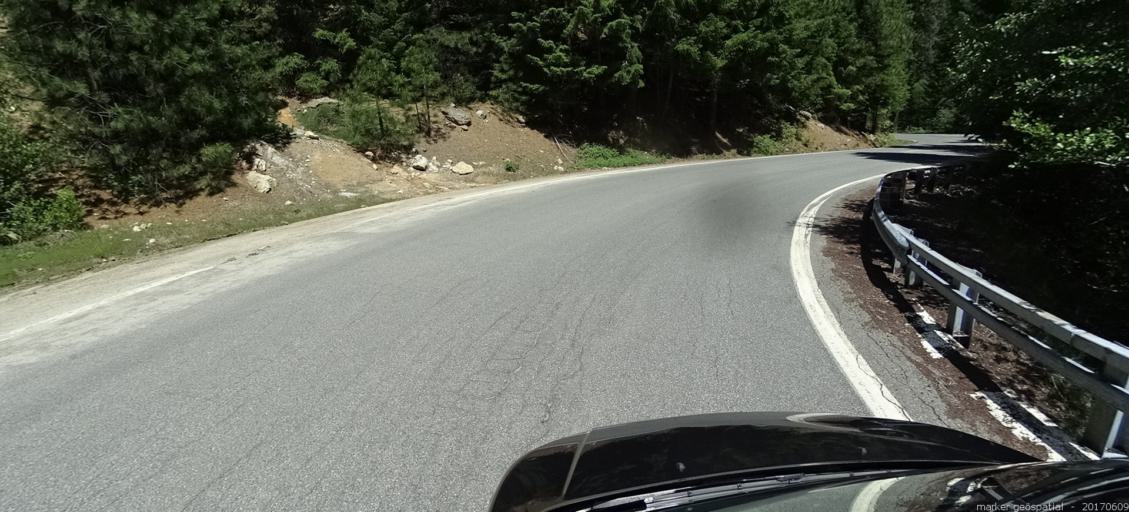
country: US
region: California
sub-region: Siskiyou County
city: Yreka
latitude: 41.4289
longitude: -122.9646
